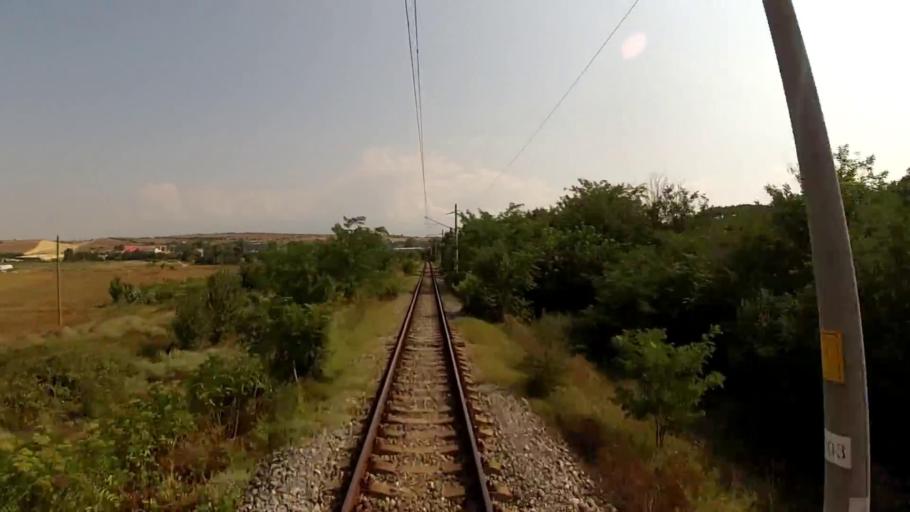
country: BG
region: Blagoevgrad
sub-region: Obshtina Petrich
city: Petrich
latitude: 41.4371
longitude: 23.3285
